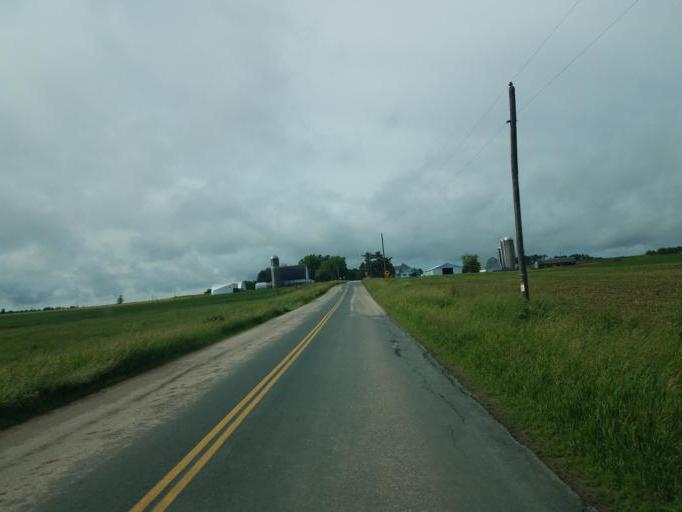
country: US
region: Wisconsin
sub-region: Monroe County
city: Tomah
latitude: 43.8074
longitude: -90.4434
